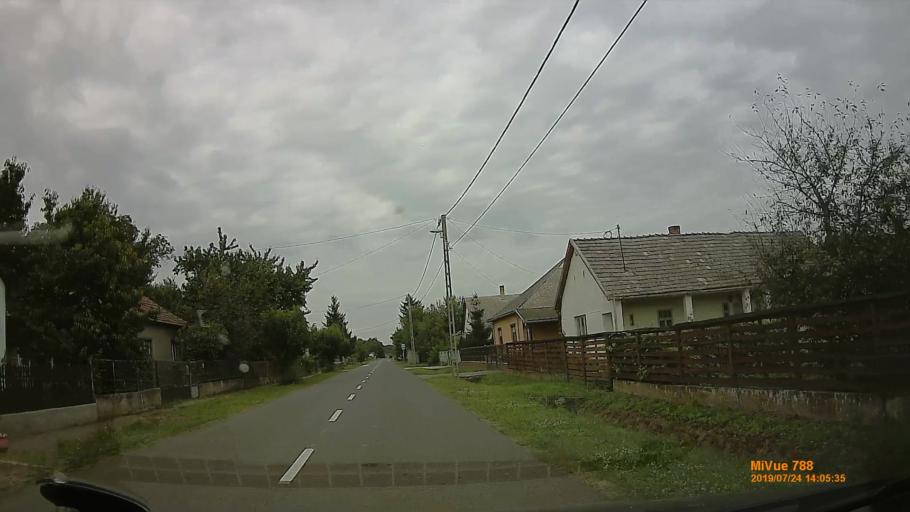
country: HU
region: Szabolcs-Szatmar-Bereg
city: Aranyosapati
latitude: 48.2883
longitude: 22.2822
